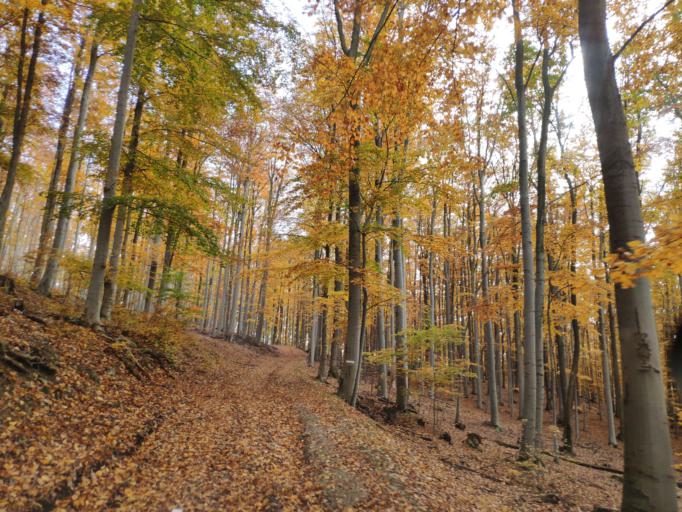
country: SK
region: Kosicky
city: Medzev
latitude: 48.7331
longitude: 20.9932
